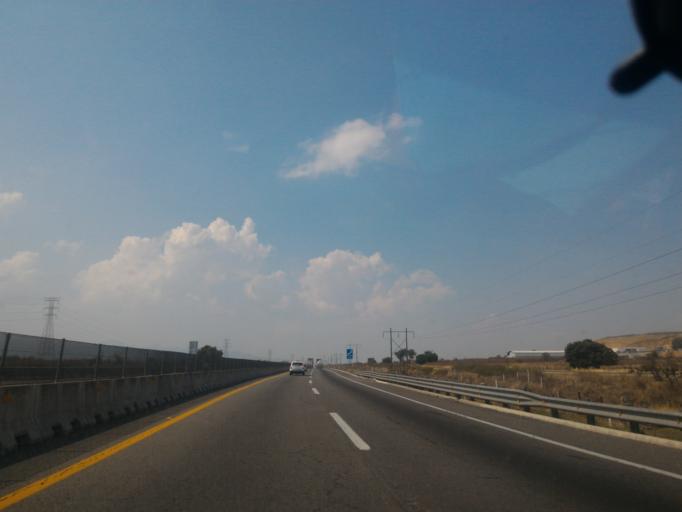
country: MX
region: Jalisco
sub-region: Zapotlan el Grande
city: Ciudad Guzman [CERESO]
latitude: 19.6488
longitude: -103.4761
